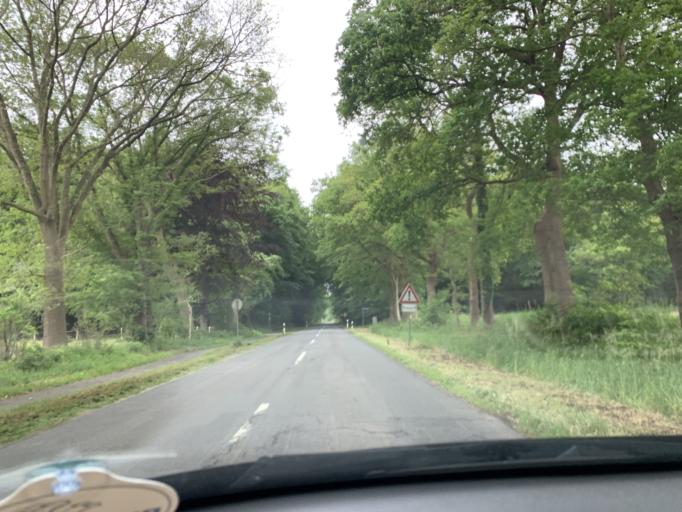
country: DE
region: Lower Saxony
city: Bockhorn
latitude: 53.3497
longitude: 8.0515
